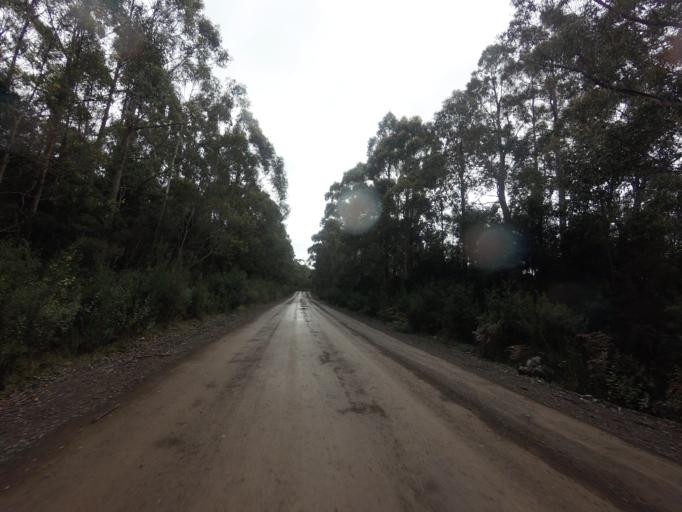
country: AU
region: Tasmania
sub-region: Huon Valley
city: Geeveston
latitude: -43.4621
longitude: 146.8999
